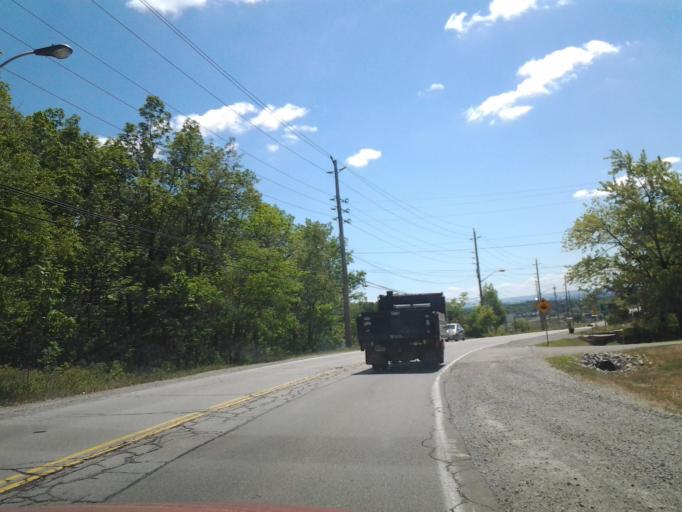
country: CA
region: Ontario
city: Hamilton
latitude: 43.3158
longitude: -79.8655
